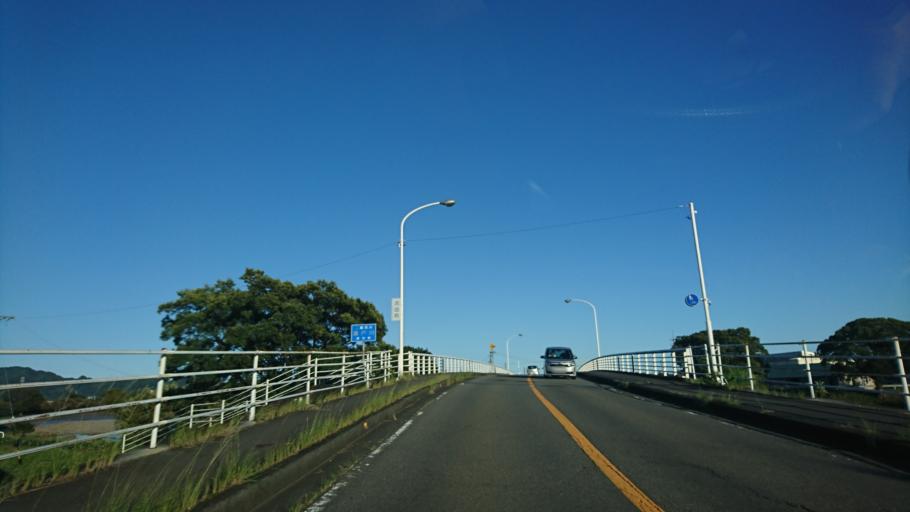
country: JP
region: Shizuoka
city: Fujieda
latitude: 34.8715
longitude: 138.2867
